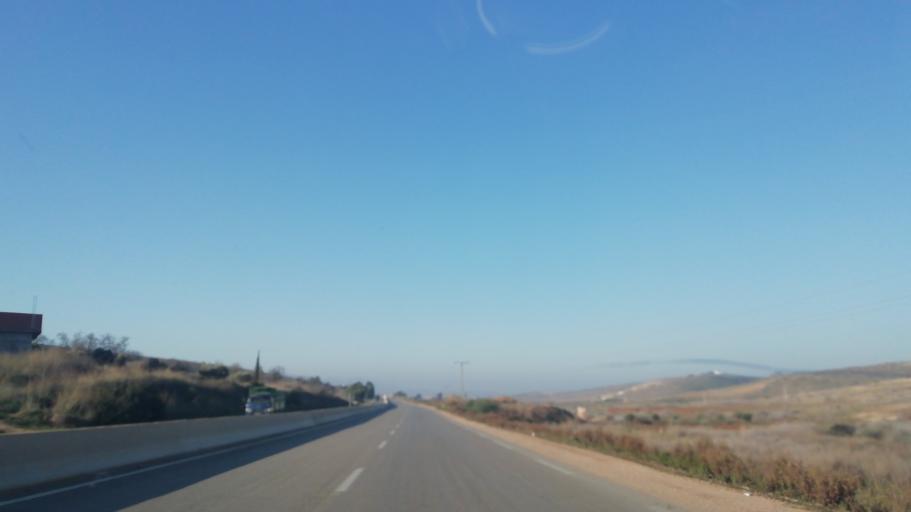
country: MA
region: Oriental
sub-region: Berkane-Taourirt
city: Ahfir
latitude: 34.9593
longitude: -2.0420
